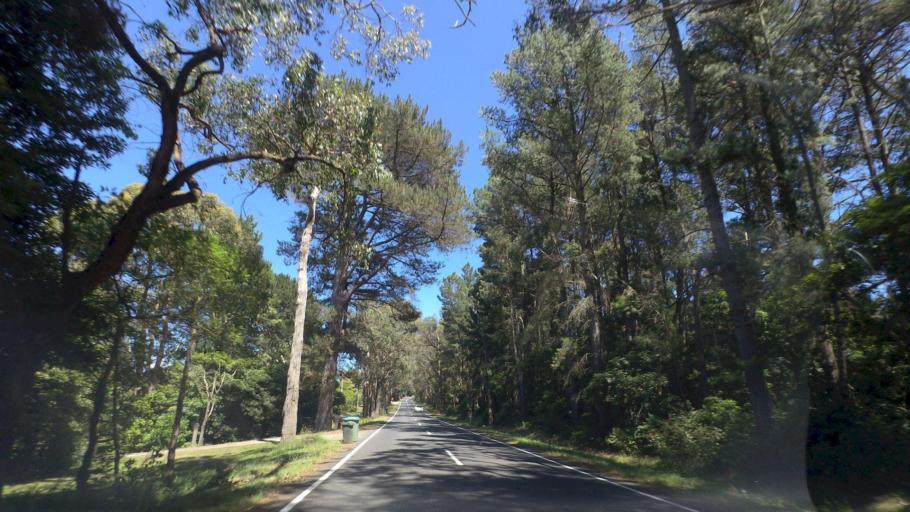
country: AU
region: Victoria
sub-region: Mornington Peninsula
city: Merricks
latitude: -38.3740
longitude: 145.0521
